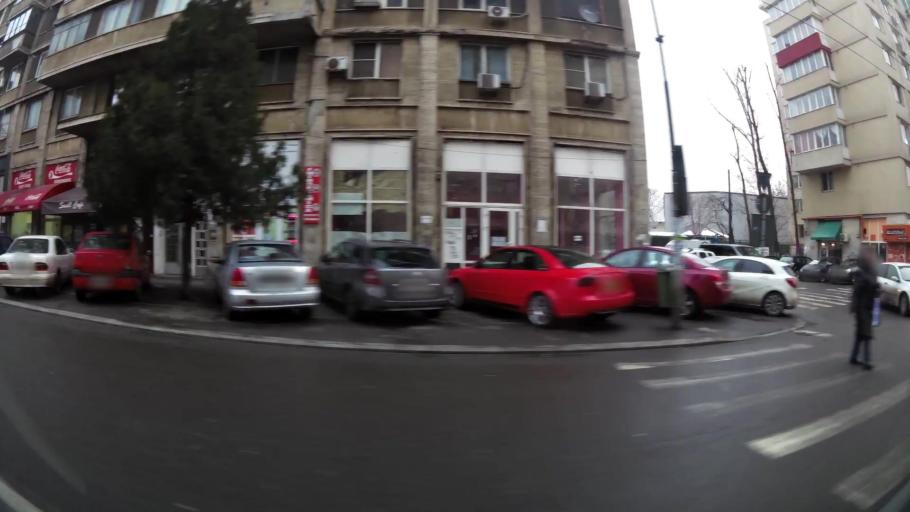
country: RO
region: Bucuresti
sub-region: Municipiul Bucuresti
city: Bucuresti
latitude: 44.4450
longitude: 26.0780
